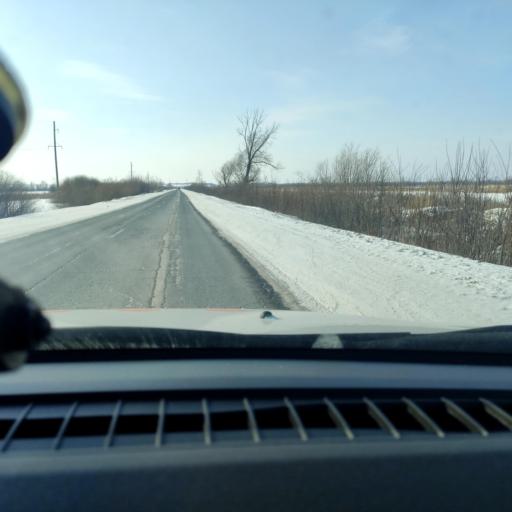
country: RU
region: Samara
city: Smyshlyayevka
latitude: 53.1550
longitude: 50.4428
